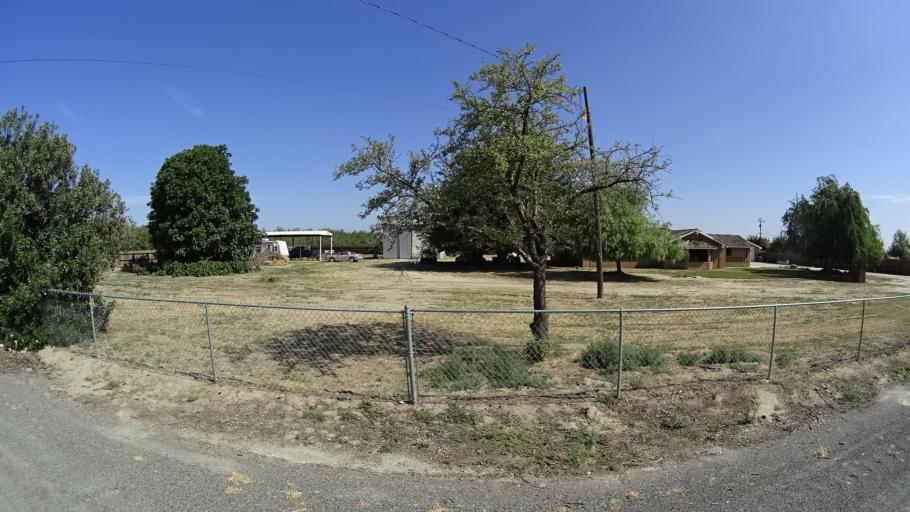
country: US
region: California
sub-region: Kings County
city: Armona
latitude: 36.2547
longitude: -119.7219
